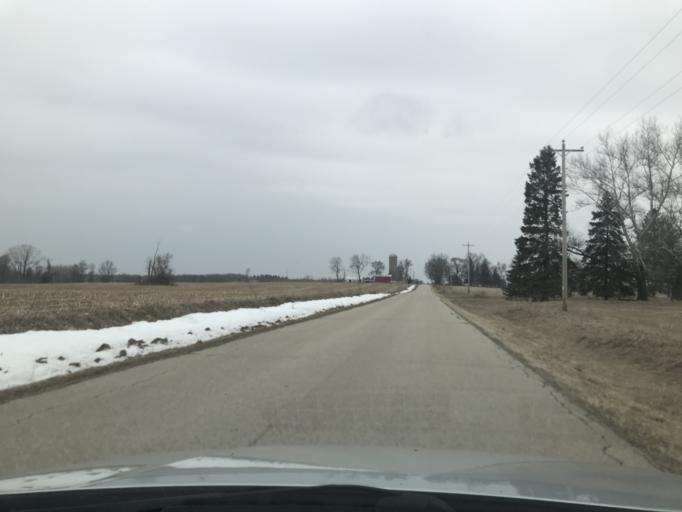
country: US
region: Wisconsin
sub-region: Marinette County
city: Peshtigo
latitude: 45.0527
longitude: -87.8509
